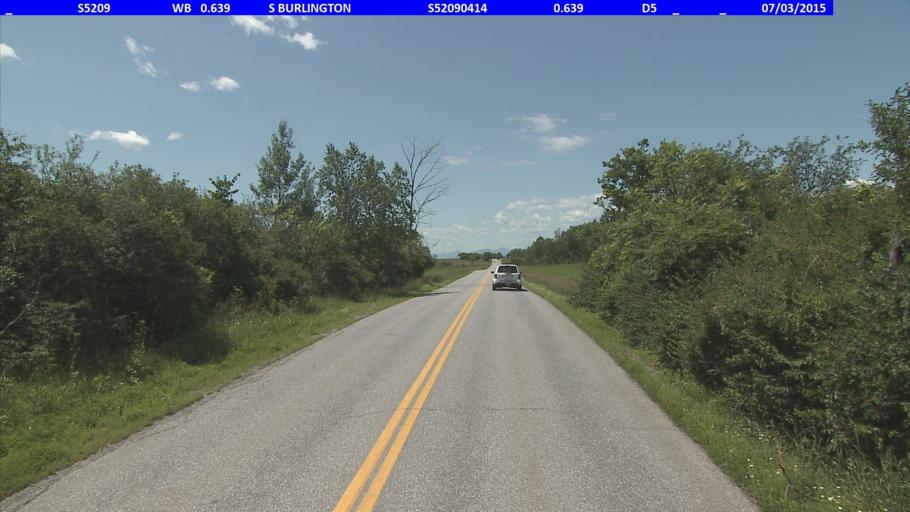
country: US
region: Vermont
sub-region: Chittenden County
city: South Burlington
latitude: 44.4124
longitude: -73.1561
